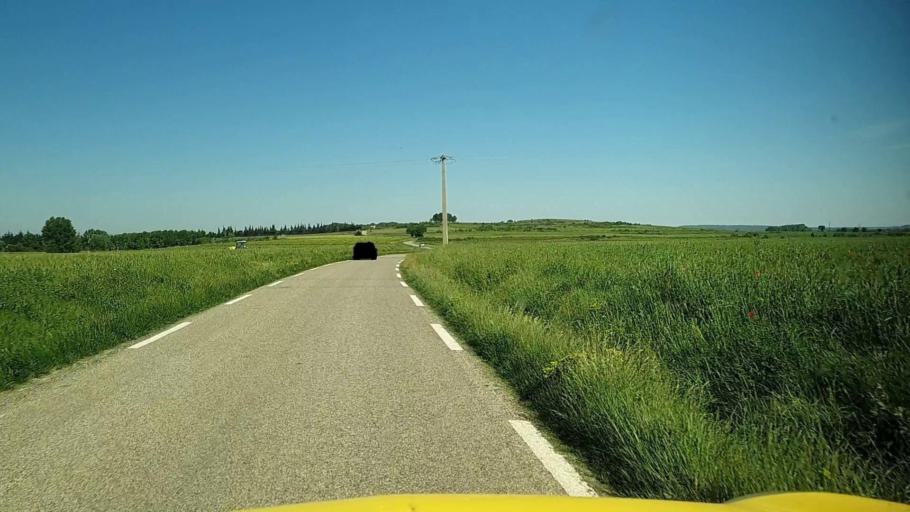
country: FR
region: Languedoc-Roussillon
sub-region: Departement du Gard
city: Saint-Chaptes
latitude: 43.9445
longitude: 4.3096
